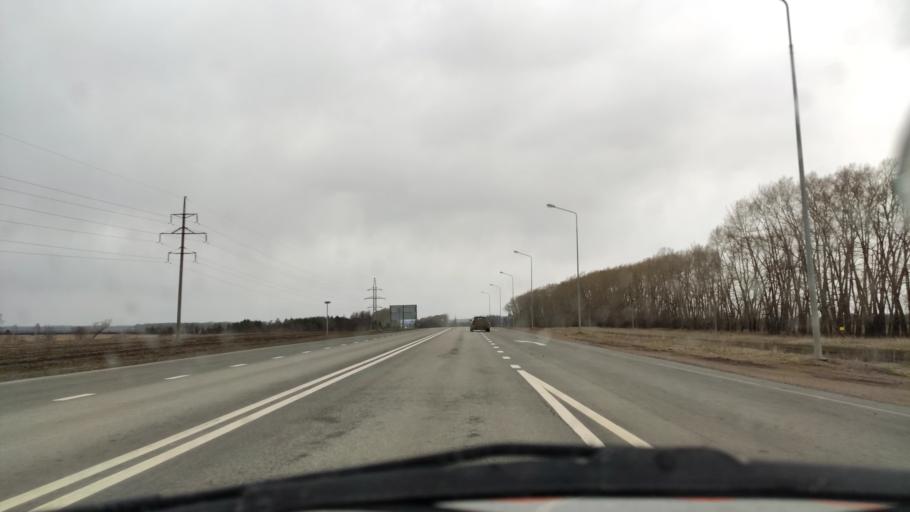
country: RU
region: Bashkortostan
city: Kushnarenkovo
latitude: 55.0662
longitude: 55.4188
